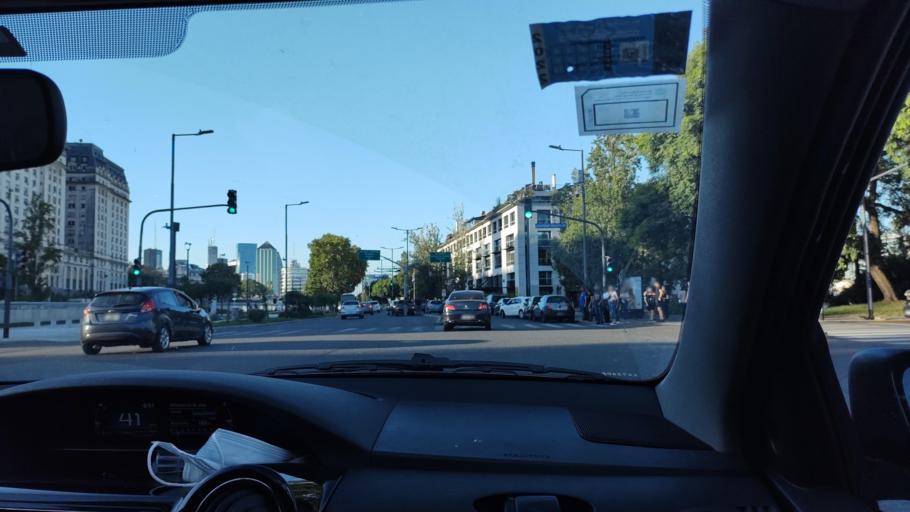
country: AR
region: Buenos Aires F.D.
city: Buenos Aires
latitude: -34.6123
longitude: -58.3662
